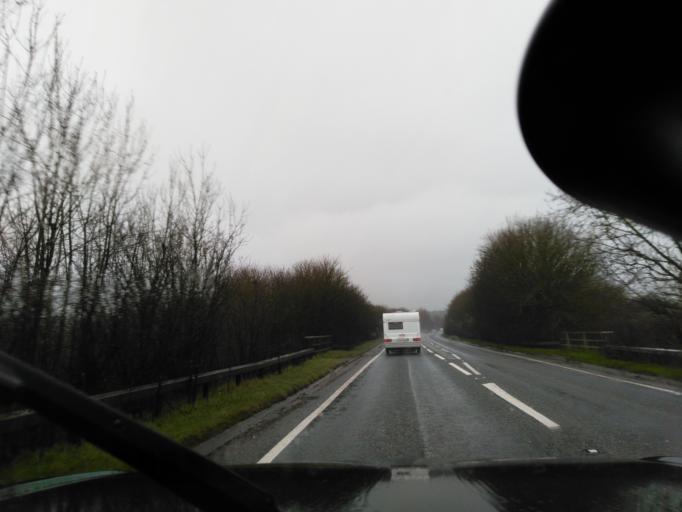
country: GB
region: England
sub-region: Somerset
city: Frome
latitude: 51.2190
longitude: -2.3047
